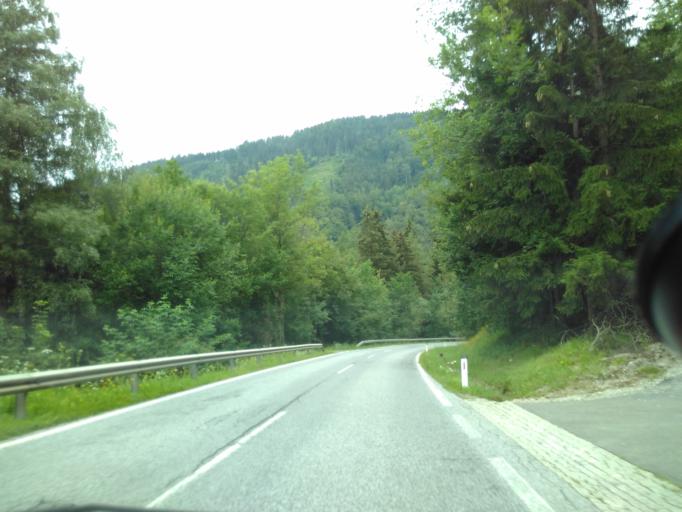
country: AT
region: Styria
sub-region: Politischer Bezirk Graz-Umgebung
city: Rothelstein
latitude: 47.2794
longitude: 15.3963
